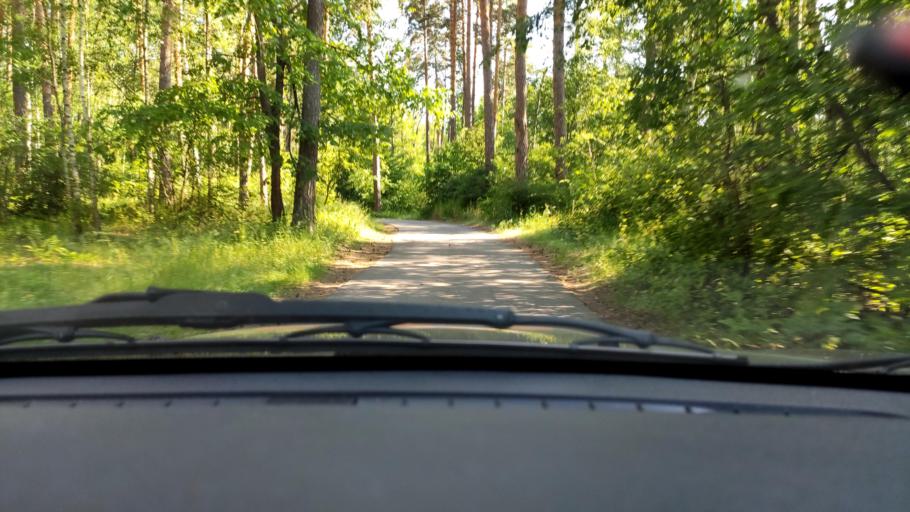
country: RU
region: Voronezj
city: Somovo
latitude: 51.8028
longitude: 39.3800
